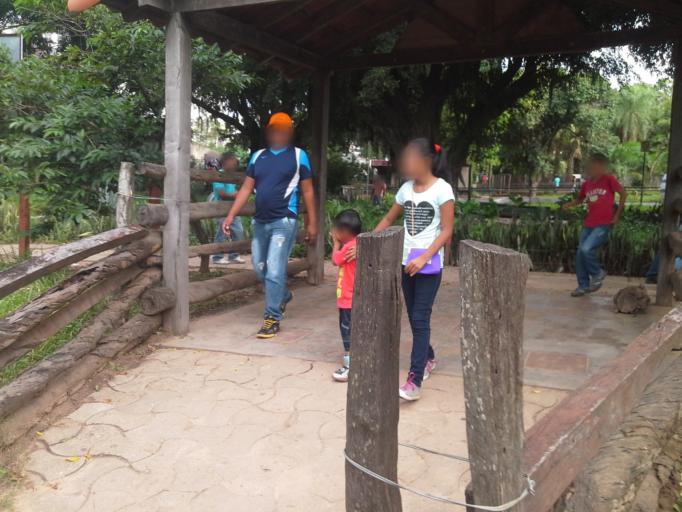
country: BO
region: Santa Cruz
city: Santa Cruz de la Sierra
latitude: -17.7597
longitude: -63.1863
